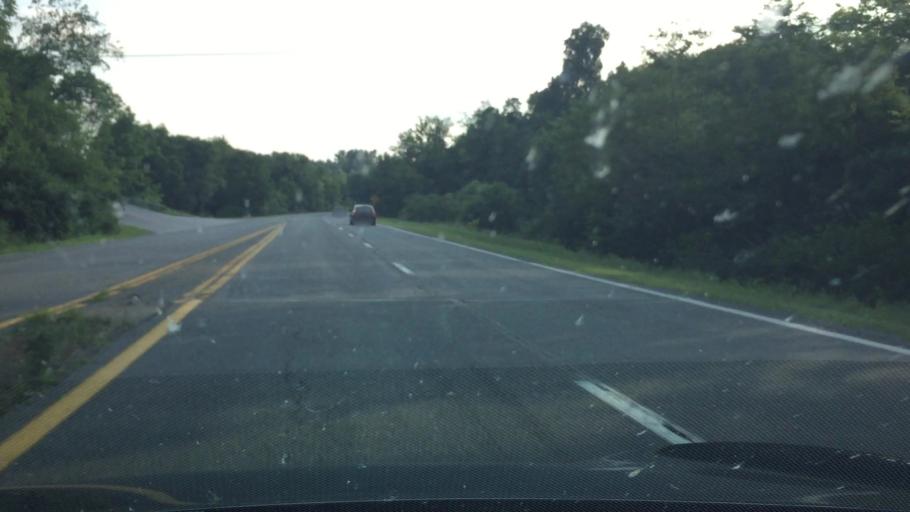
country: US
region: Virginia
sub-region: City of Radford
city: Radford
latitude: 37.1357
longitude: -80.6152
